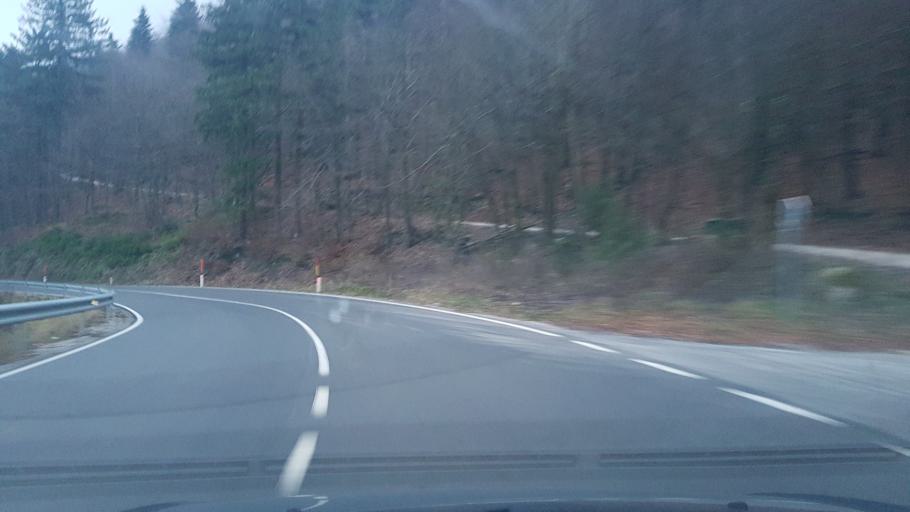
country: SI
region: Idrija
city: Idrija
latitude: 45.9216
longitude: 14.0394
